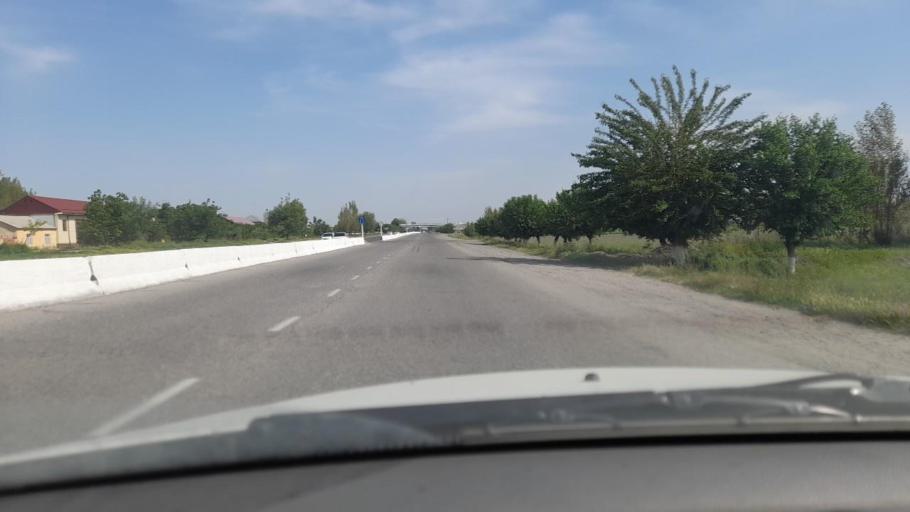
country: UZ
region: Samarqand
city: Daxbet
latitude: 39.7757
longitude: 66.8917
